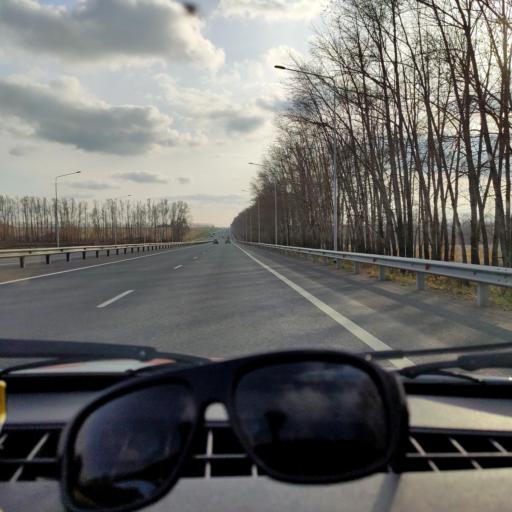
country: RU
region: Bashkortostan
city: Karmaskaly
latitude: 54.3419
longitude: 55.9033
